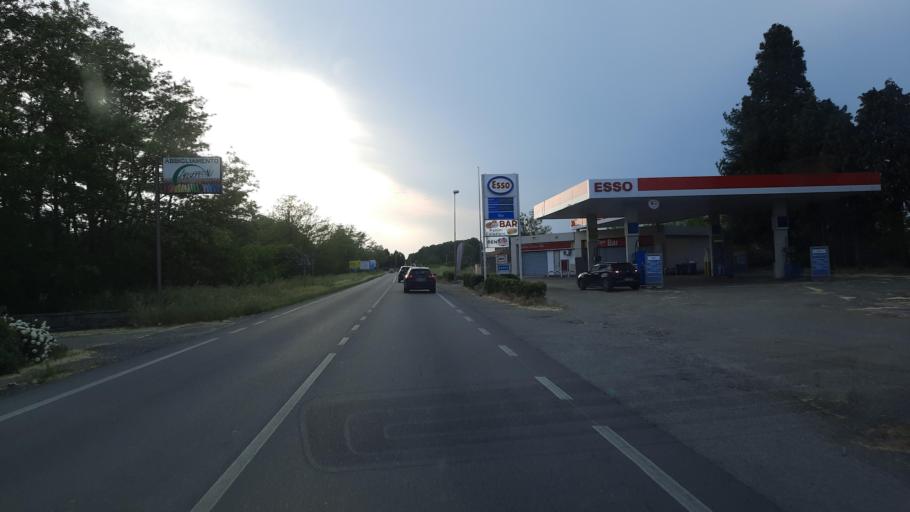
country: IT
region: Lombardy
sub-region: Provincia di Pavia
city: Garlasco
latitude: 45.1907
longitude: 8.9419
